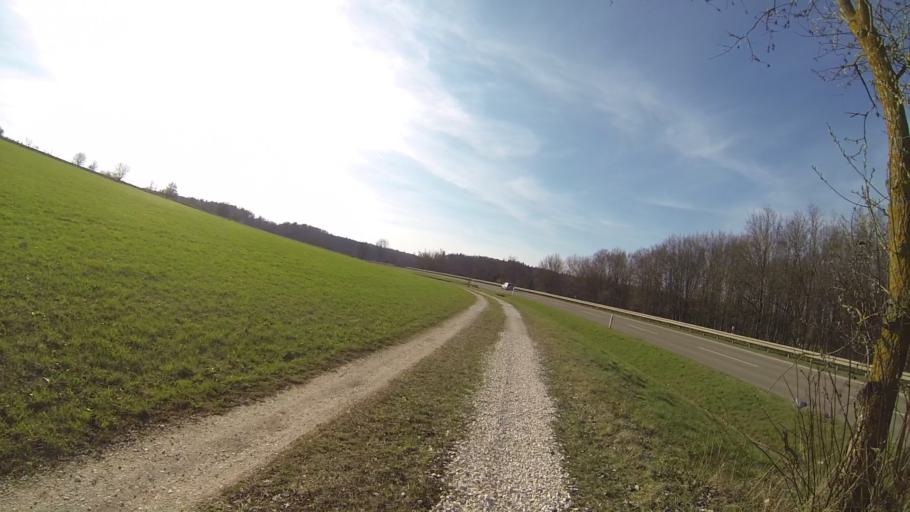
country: DE
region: Baden-Wuerttemberg
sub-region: Regierungsbezirk Stuttgart
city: Hermaringen
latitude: 48.5820
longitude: 10.2231
